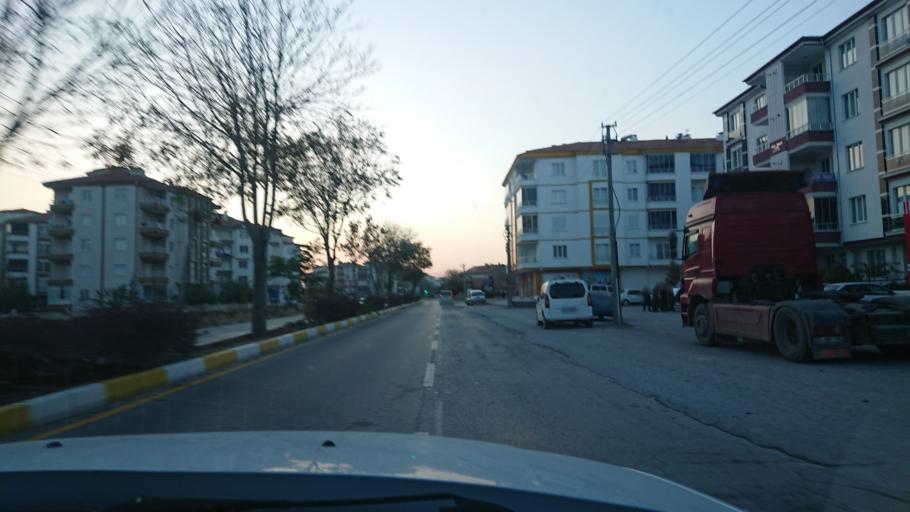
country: TR
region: Aksaray
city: Aksaray
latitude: 38.3603
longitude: 34.0110
